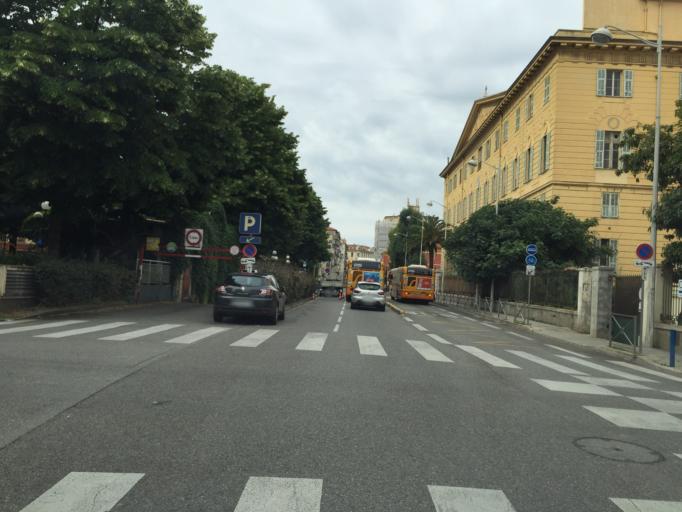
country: FR
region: Provence-Alpes-Cote d'Azur
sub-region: Departement des Alpes-Maritimes
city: Nice
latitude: 43.7031
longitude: 7.2758
